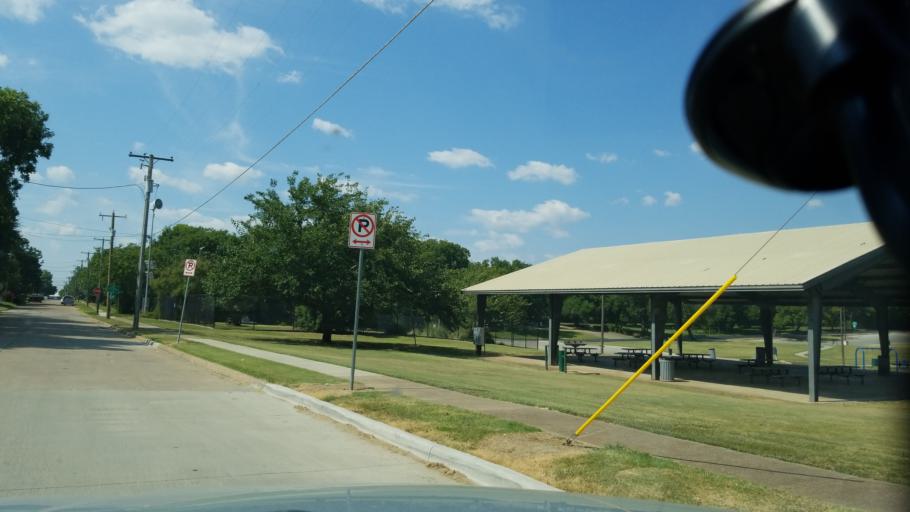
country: US
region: Texas
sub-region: Dallas County
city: Grand Prairie
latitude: 32.7563
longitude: -96.9630
